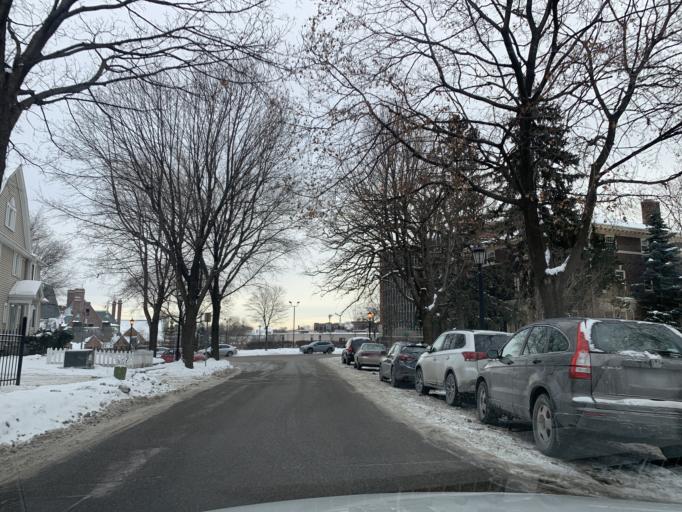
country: US
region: Minnesota
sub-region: Hennepin County
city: Minneapolis
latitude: 44.9638
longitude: -93.2816
